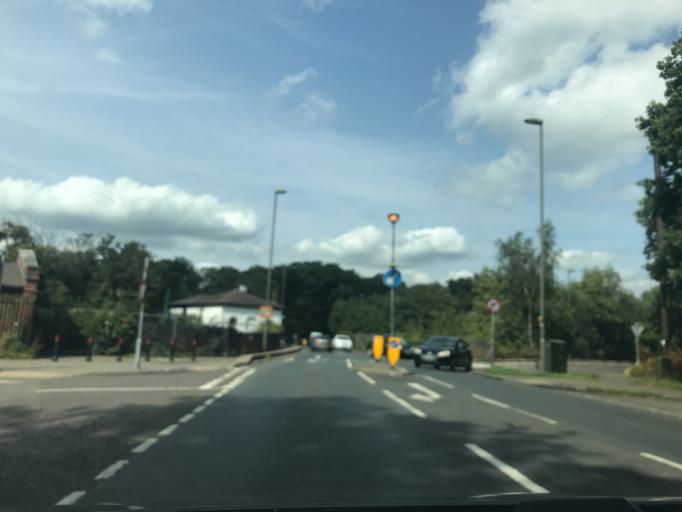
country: GB
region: England
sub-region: Surrey
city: Weybridge
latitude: 51.3613
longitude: -0.4565
